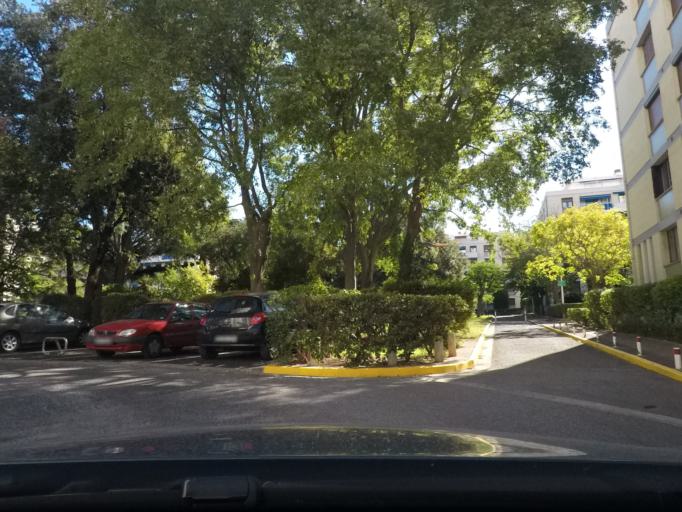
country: FR
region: Provence-Alpes-Cote d'Azur
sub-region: Departement des Bouches-du-Rhone
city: Marseille 09
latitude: 43.2545
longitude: 5.4172
